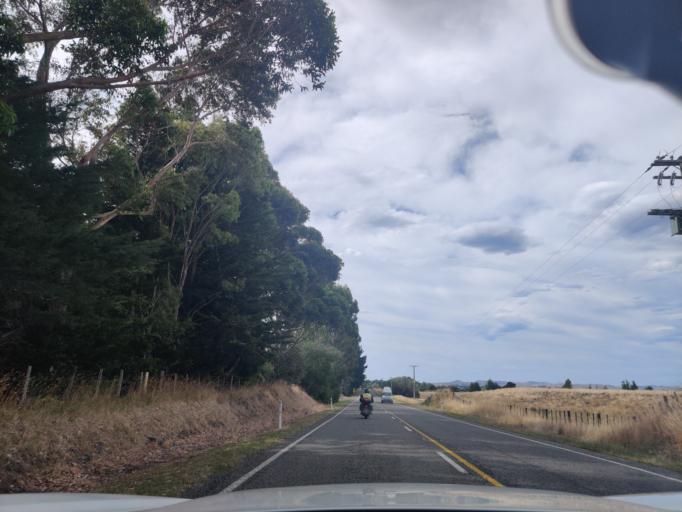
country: NZ
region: Wellington
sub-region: Masterton District
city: Masterton
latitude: -40.8758
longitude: 175.6530
